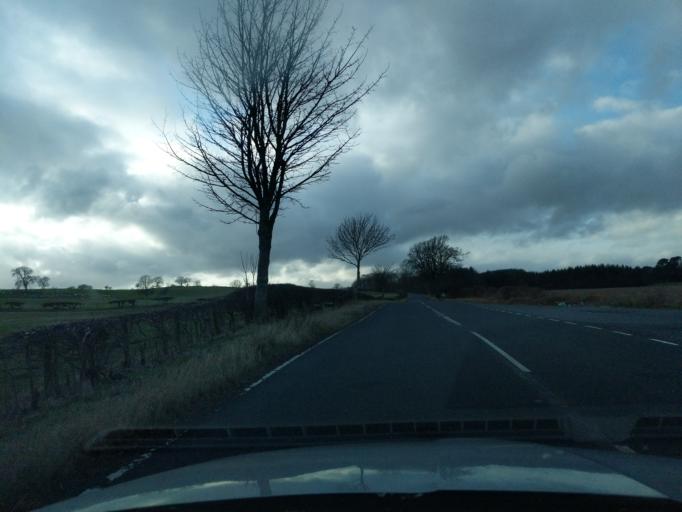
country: GB
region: England
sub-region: North Yorkshire
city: Catterick Garrison
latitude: 54.3457
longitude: -1.7312
